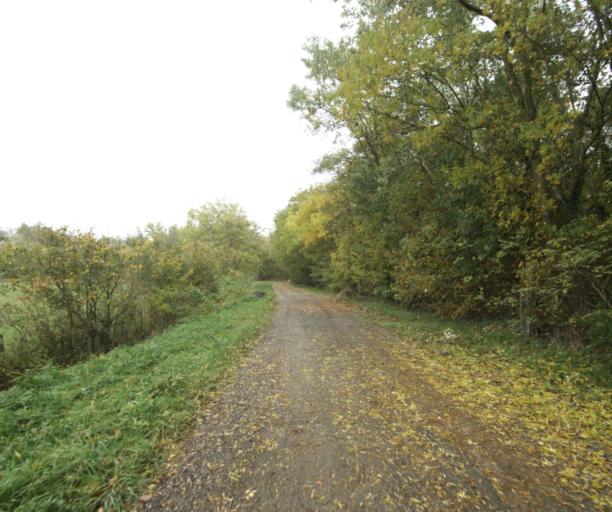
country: FR
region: Rhone-Alpes
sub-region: Departement de l'Ain
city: Pont-de-Vaux
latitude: 46.4594
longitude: 4.8970
